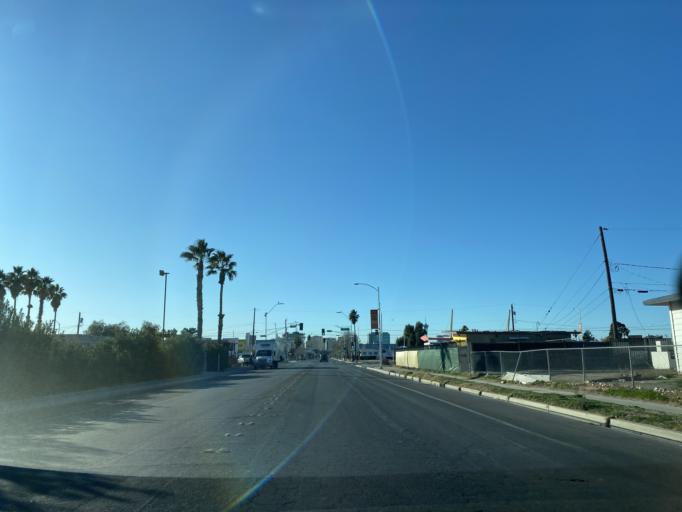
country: US
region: Nevada
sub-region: Clark County
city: Las Vegas
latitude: 36.1894
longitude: -115.1473
